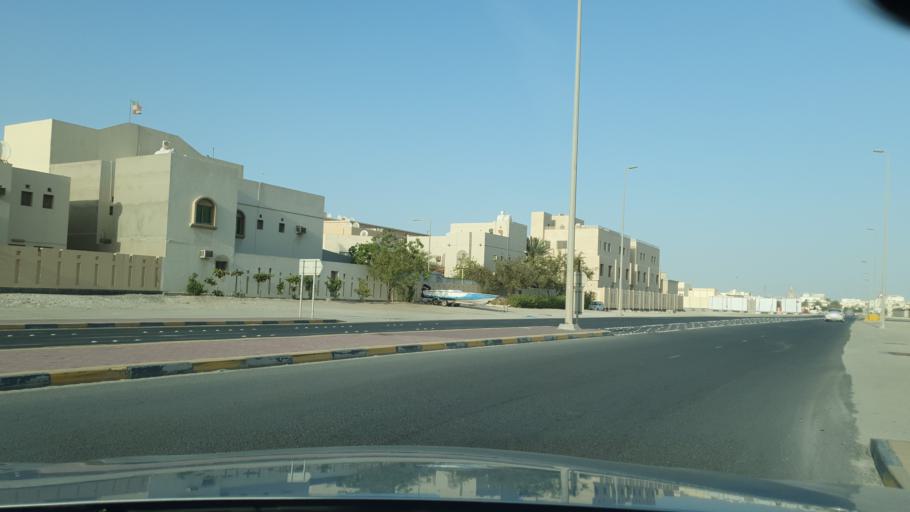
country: BH
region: Muharraq
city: Al Muharraq
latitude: 26.2665
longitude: 50.5983
